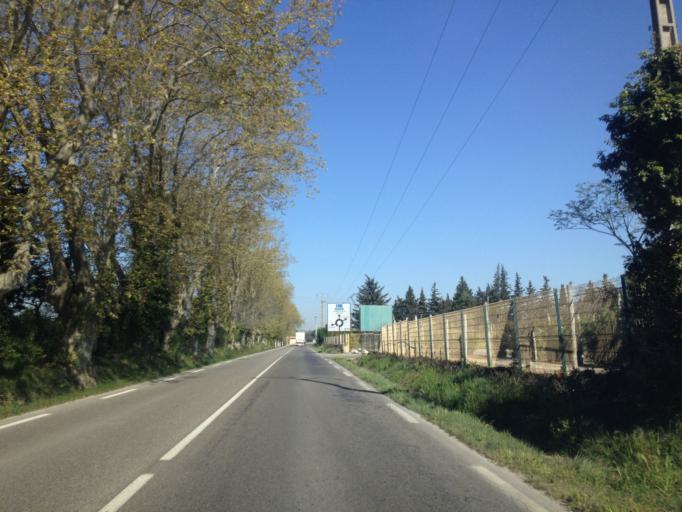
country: FR
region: Provence-Alpes-Cote d'Azur
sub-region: Departement du Vaucluse
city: Sarrians
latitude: 44.0953
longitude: 4.9483
